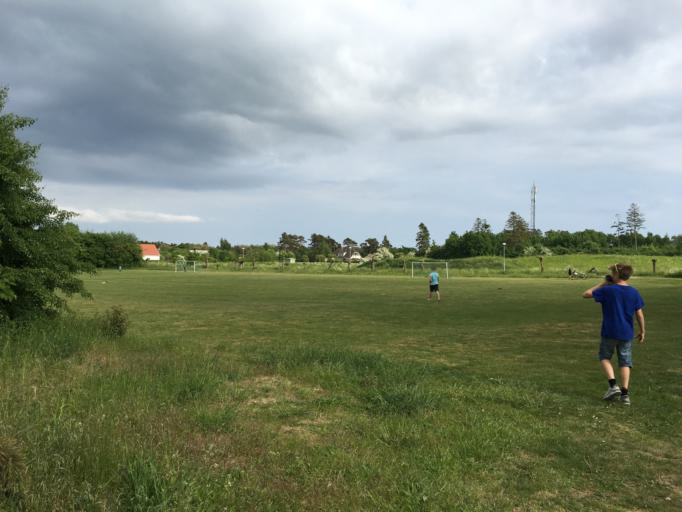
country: SE
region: Skane
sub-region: Vellinge Kommun
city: Hollviken
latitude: 55.4214
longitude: 12.9742
